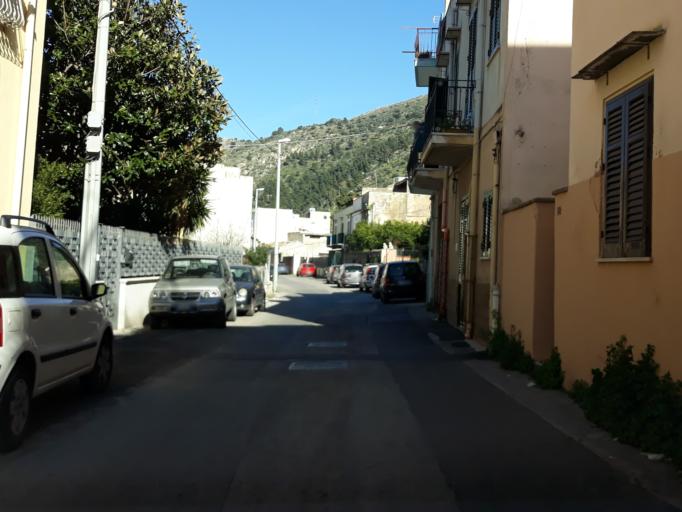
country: IT
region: Sicily
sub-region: Palermo
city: Ciaculli
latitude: 38.0788
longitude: 13.3708
